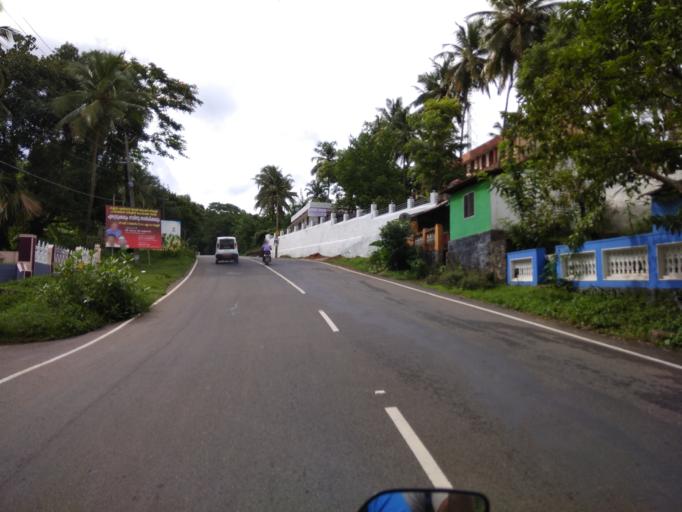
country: IN
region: Kerala
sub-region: Thrissur District
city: Trichur
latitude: 10.5349
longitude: 76.3384
